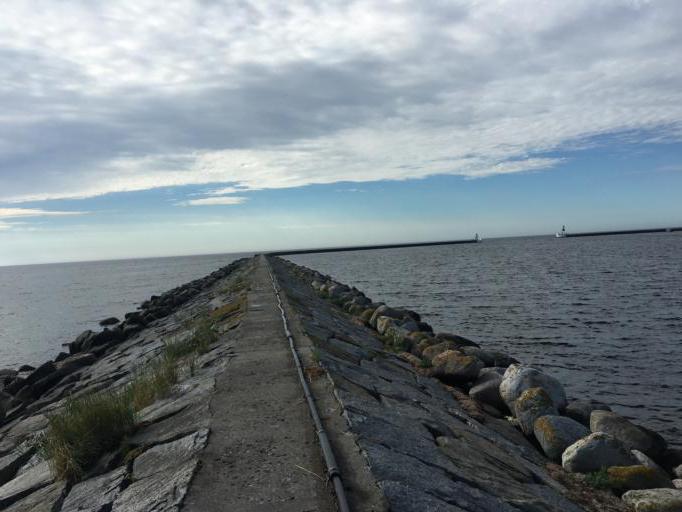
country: SE
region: Skane
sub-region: Vellinge Kommun
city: Hollviken
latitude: 55.3978
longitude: 12.9490
